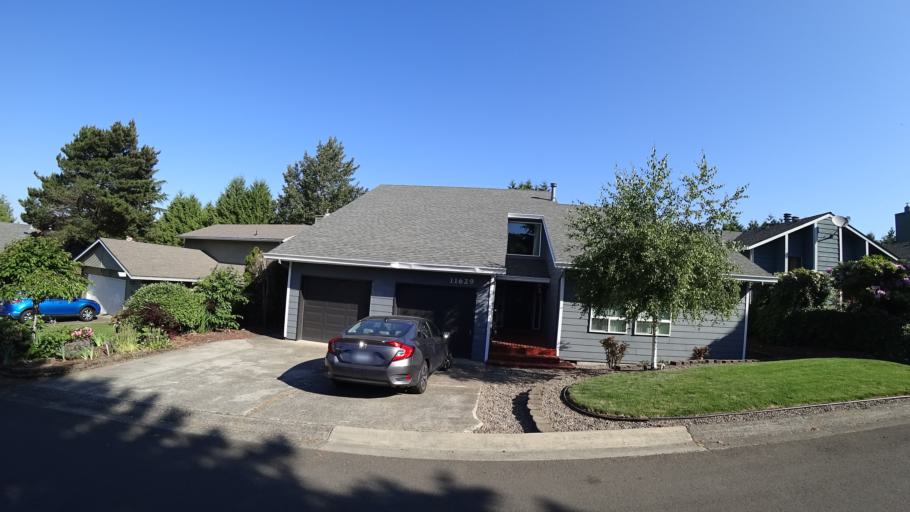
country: US
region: Oregon
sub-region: Multnomah County
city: Lents
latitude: 45.4699
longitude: -122.5443
